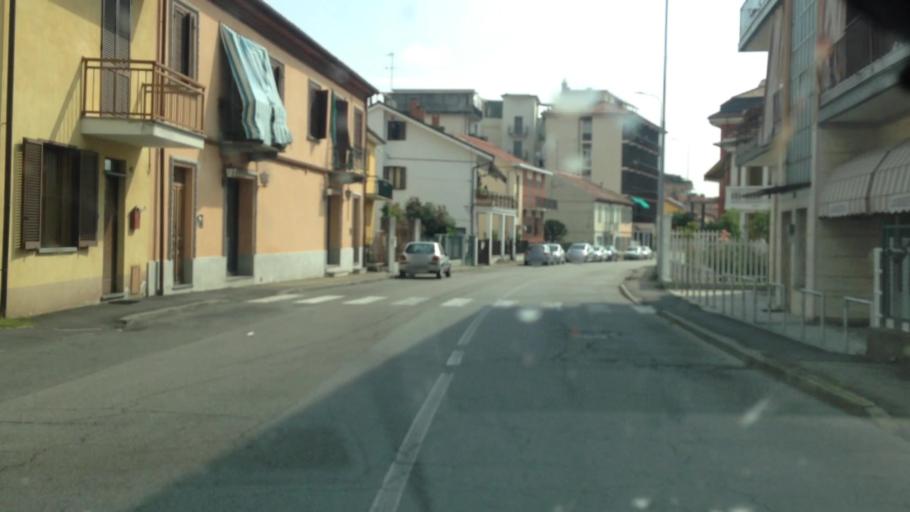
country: IT
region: Piedmont
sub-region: Provincia di Asti
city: Asti
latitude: 44.9076
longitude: 8.2125
